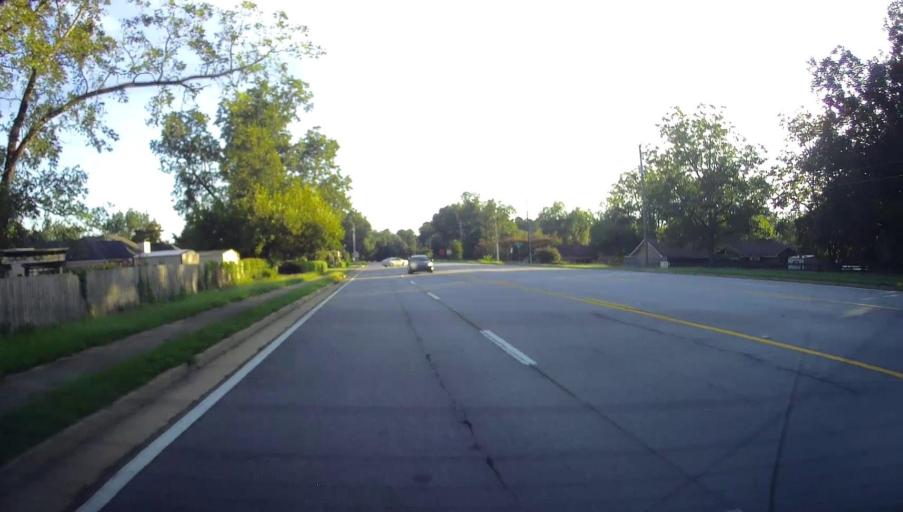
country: US
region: Georgia
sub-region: Muscogee County
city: Columbus
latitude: 32.5054
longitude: -84.8968
